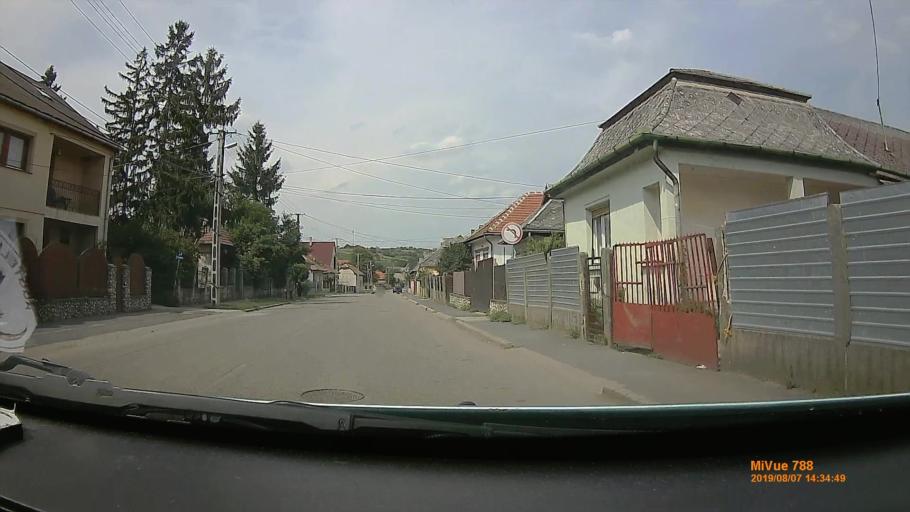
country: HU
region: Borsod-Abauj-Zemplen
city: Szikszo
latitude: 48.2029
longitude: 20.9264
